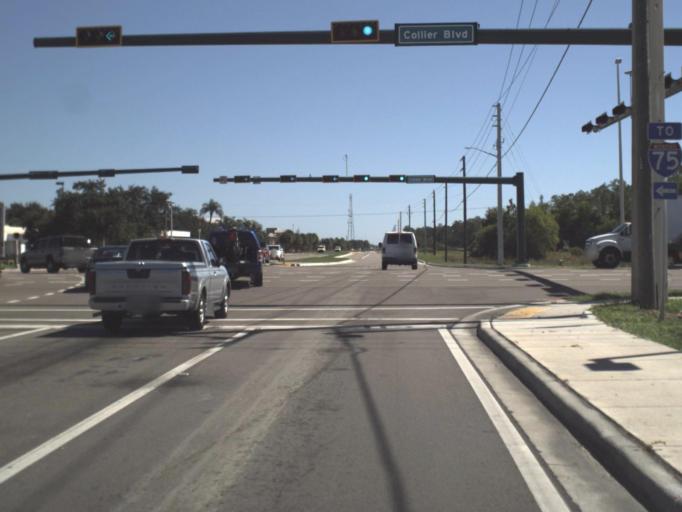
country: US
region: Florida
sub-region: Collier County
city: Golden Gate
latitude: 26.1548
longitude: -81.6870
